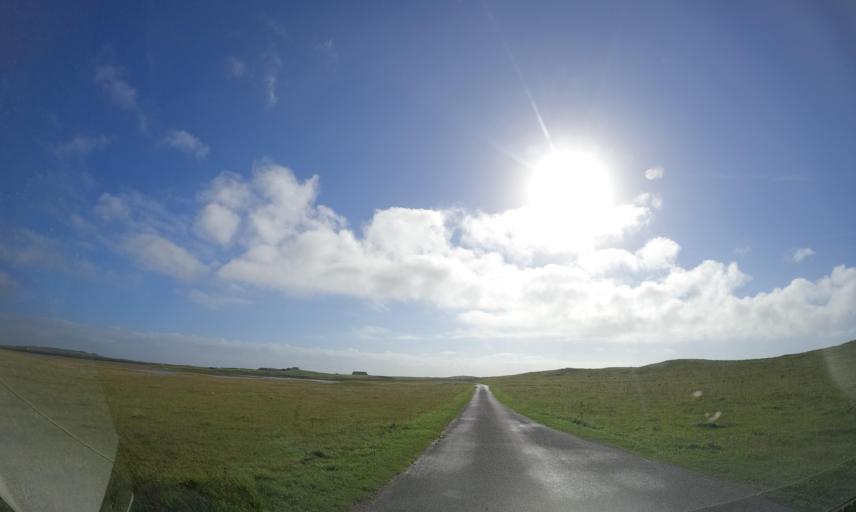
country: GB
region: Scotland
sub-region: Eilean Siar
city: Barra
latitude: 56.4940
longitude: -6.8528
